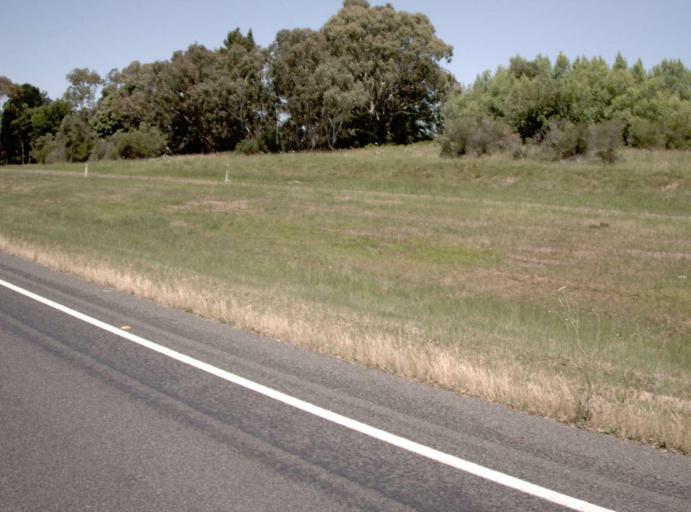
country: AU
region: Victoria
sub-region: Baw Baw
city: Warragul
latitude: -38.1096
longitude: 145.8589
